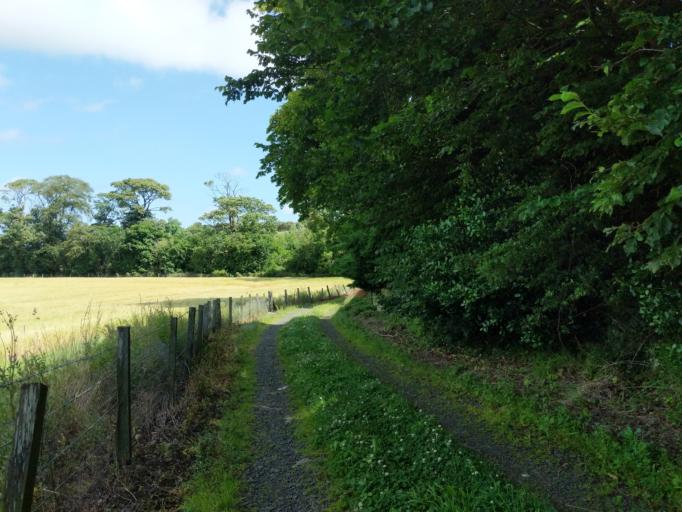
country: GB
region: Scotland
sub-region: Edinburgh
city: Currie
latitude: 55.9304
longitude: -3.3332
